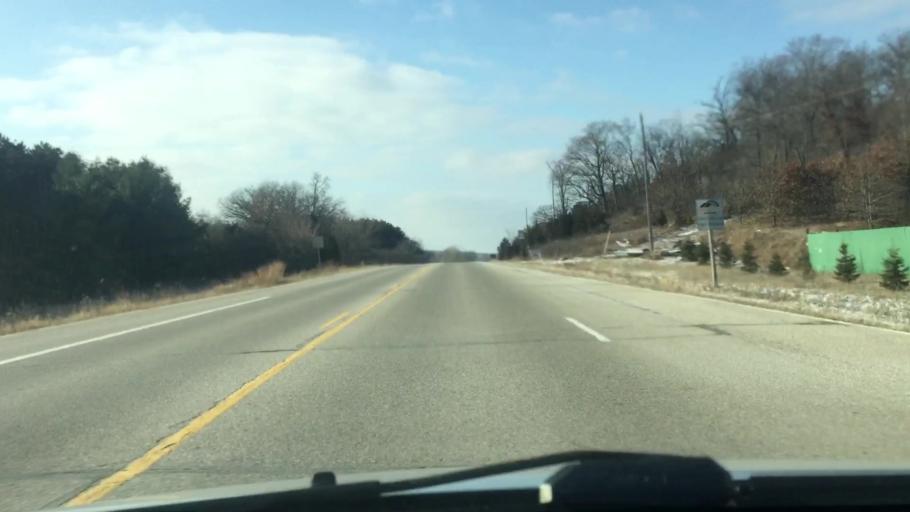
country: US
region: Wisconsin
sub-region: Waukesha County
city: Eagle
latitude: 42.8791
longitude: -88.5060
